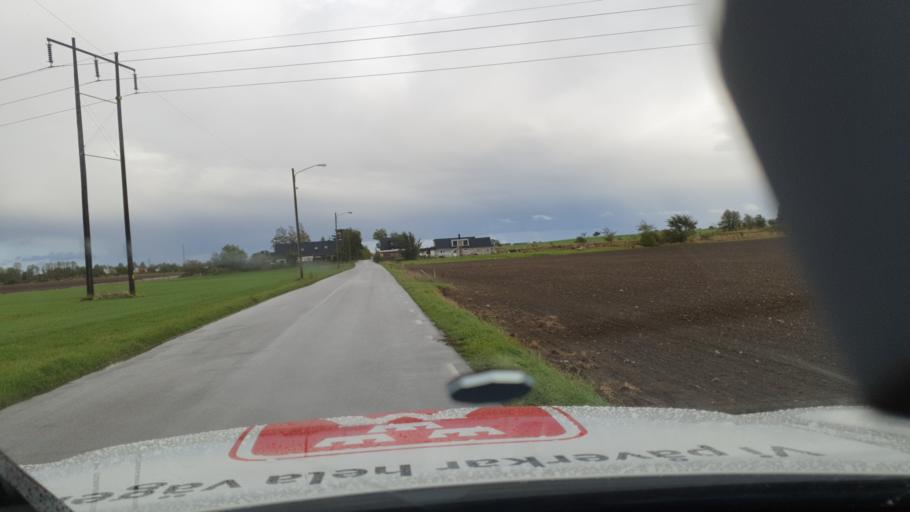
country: SE
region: Skane
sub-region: Malmo
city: Tygelsjo
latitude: 55.5243
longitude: 13.0480
